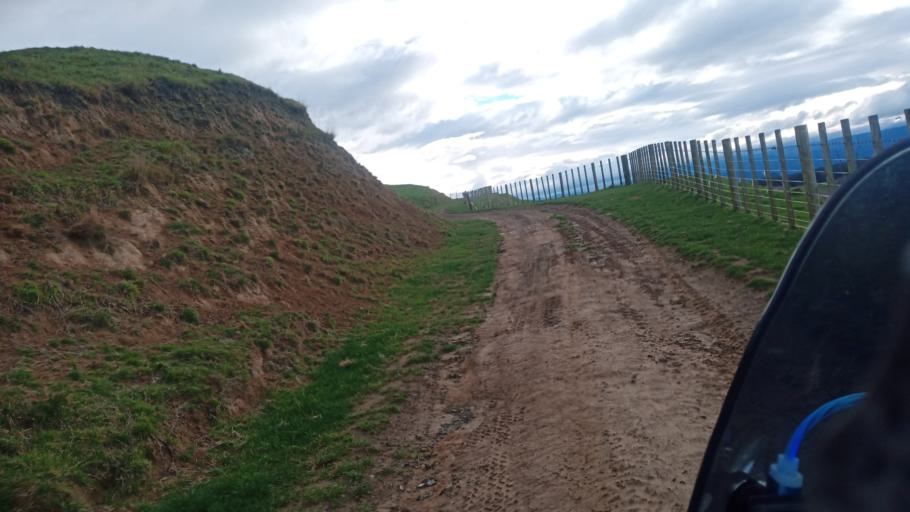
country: NZ
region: Gisborne
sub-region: Gisborne District
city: Gisborne
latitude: -38.3402
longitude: 177.9118
